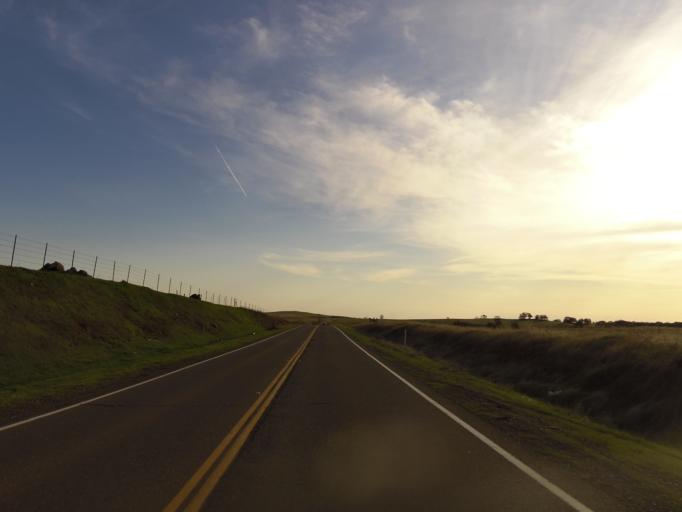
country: US
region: California
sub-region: El Dorado County
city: El Dorado Hills
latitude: 38.6348
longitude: -121.1143
